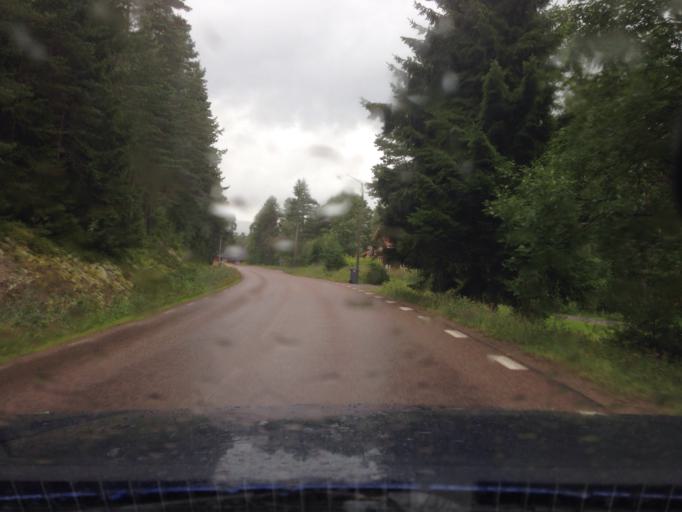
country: SE
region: Dalarna
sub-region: Ludvika Kommun
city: Grangesberg
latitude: 60.1367
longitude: 15.0032
